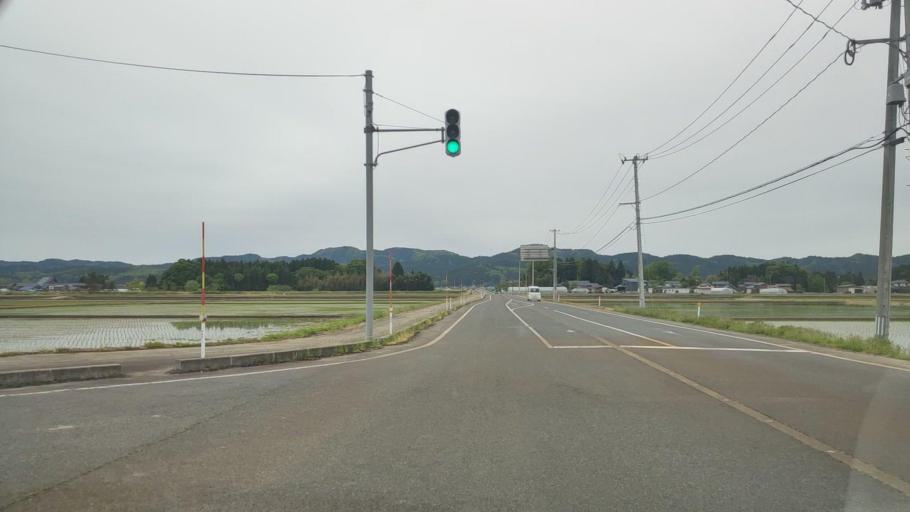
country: JP
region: Niigata
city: Gosen
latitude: 37.7289
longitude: 139.1617
